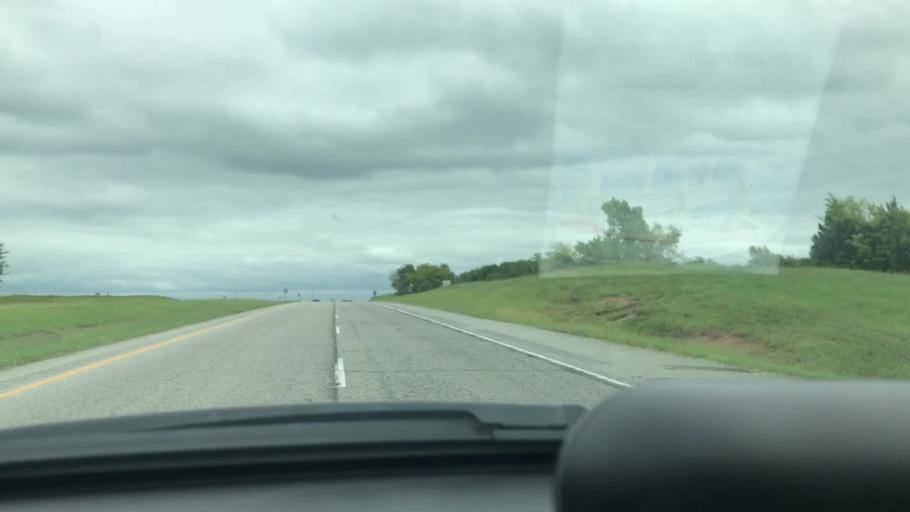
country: US
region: Oklahoma
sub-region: Wagoner County
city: Wagoner
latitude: 35.9901
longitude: -95.3729
